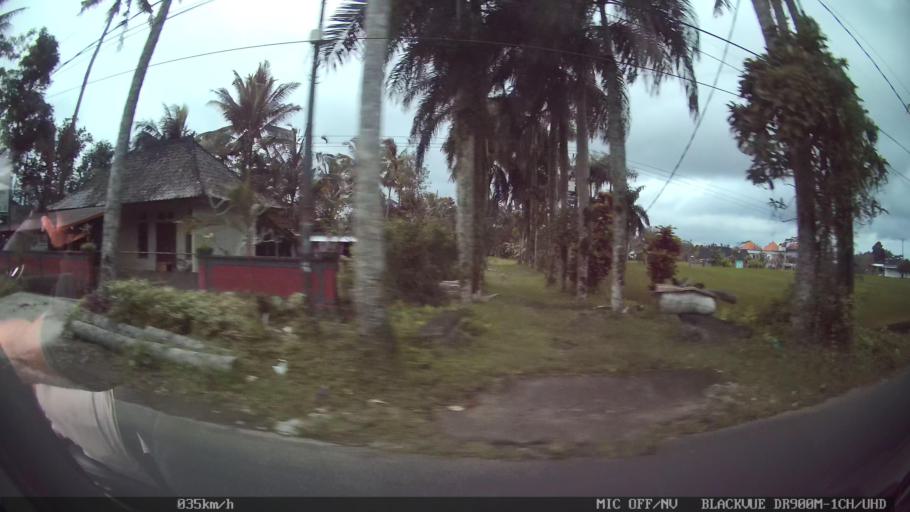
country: ID
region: Bali
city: Banjar Triwangsakeliki
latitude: -8.4625
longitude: 115.2592
